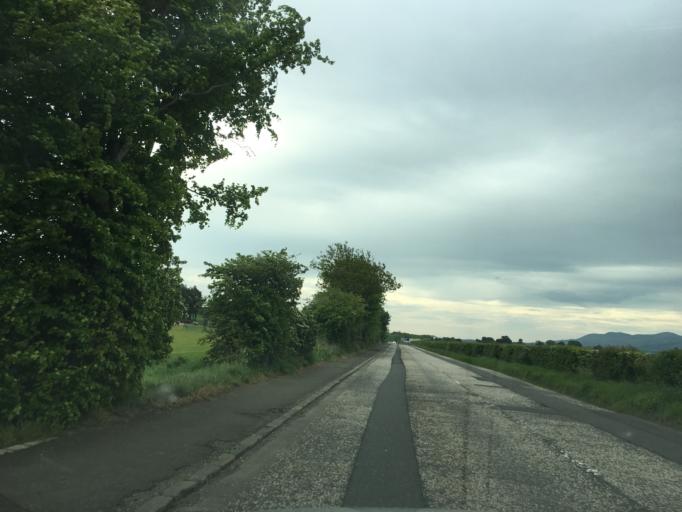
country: GB
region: Scotland
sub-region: Edinburgh
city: Ratho
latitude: 55.9511
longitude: -3.3396
